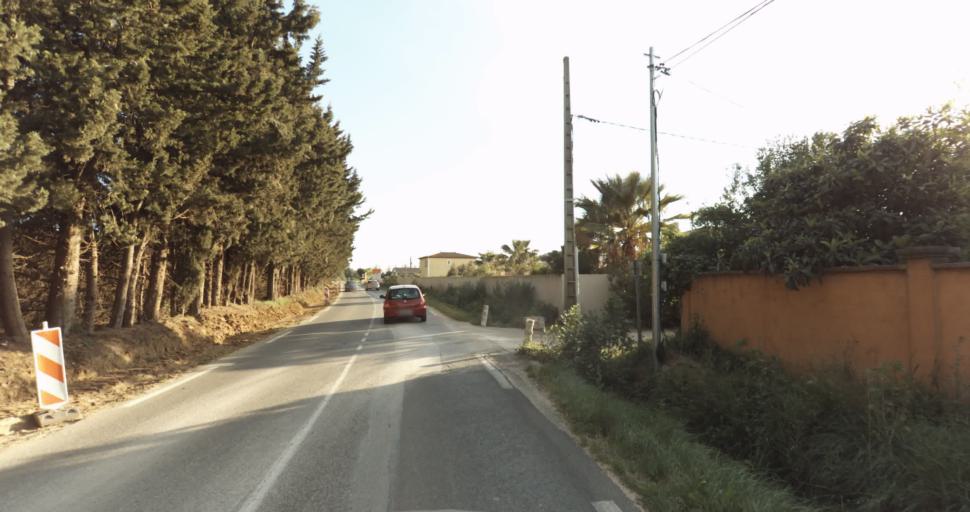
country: FR
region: Provence-Alpes-Cote d'Azur
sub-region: Departement du Var
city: La Crau
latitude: 43.1615
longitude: 6.0993
